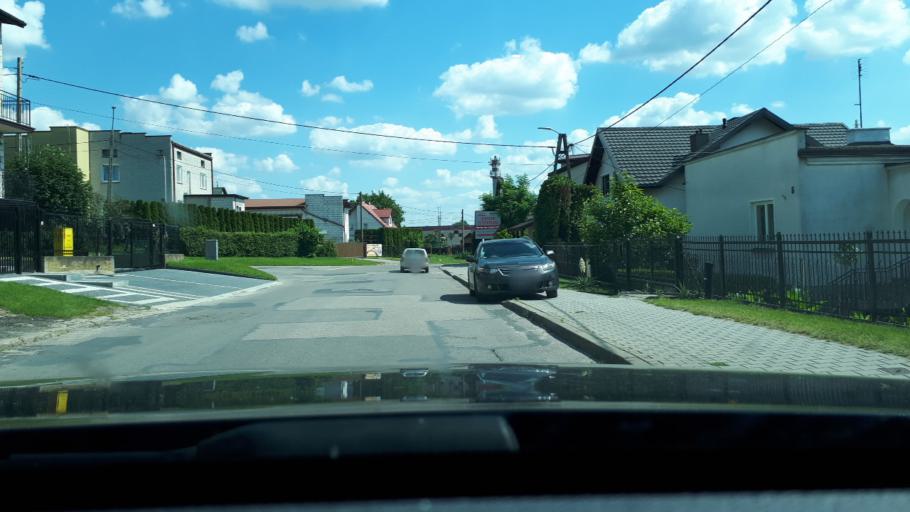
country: PL
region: Masovian Voivodeship
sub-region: Powiat grojecki
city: Warka
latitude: 51.7884
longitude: 21.1962
